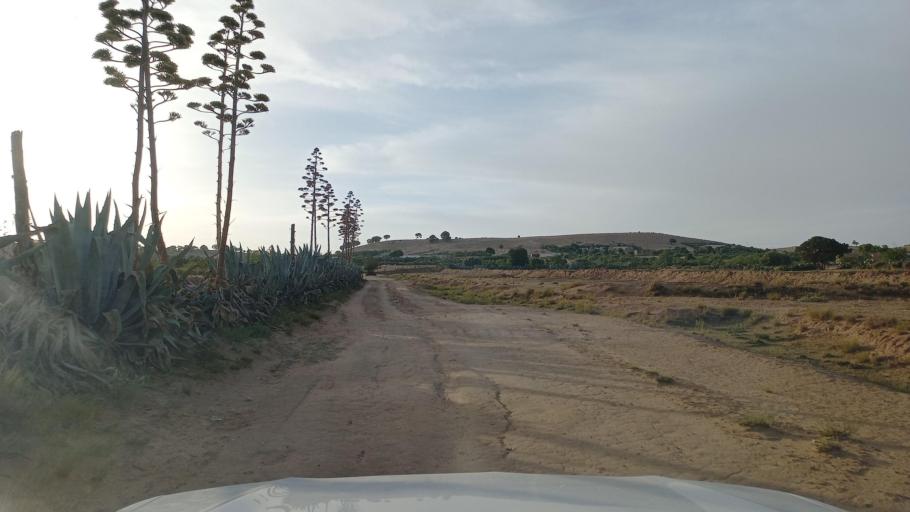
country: TN
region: Al Qasrayn
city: Sbiba
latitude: 35.4080
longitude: 8.9060
